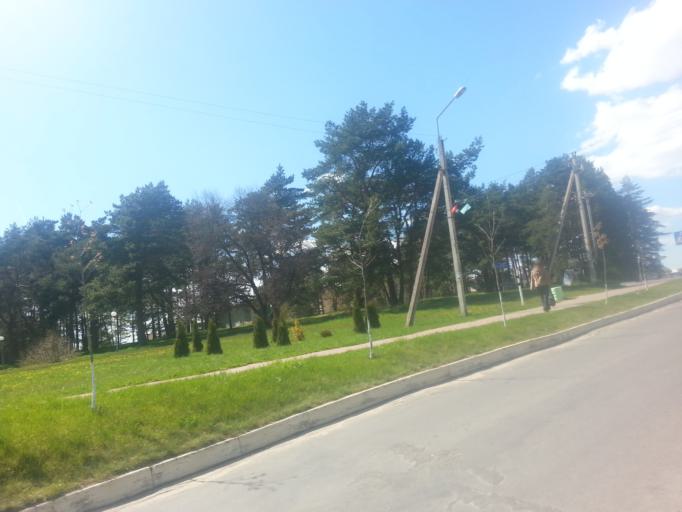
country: BY
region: Minsk
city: Narach
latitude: 54.9139
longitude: 26.7070
